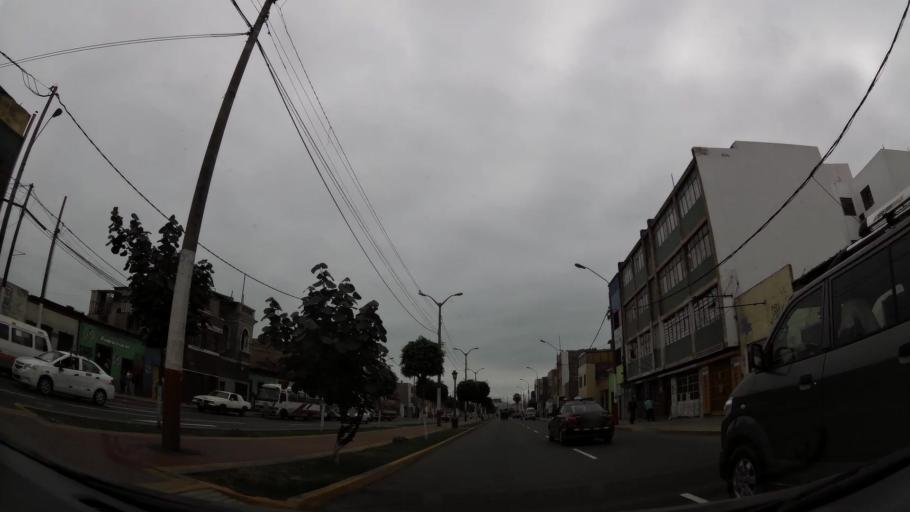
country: PE
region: Callao
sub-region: Callao
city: Callao
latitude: -12.0626
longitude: -77.1395
